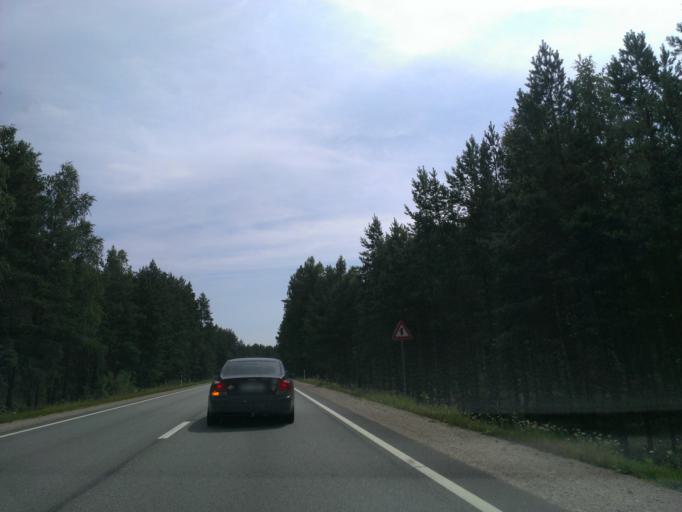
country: LV
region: Riga
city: Bergi
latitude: 56.9615
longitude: 24.3733
